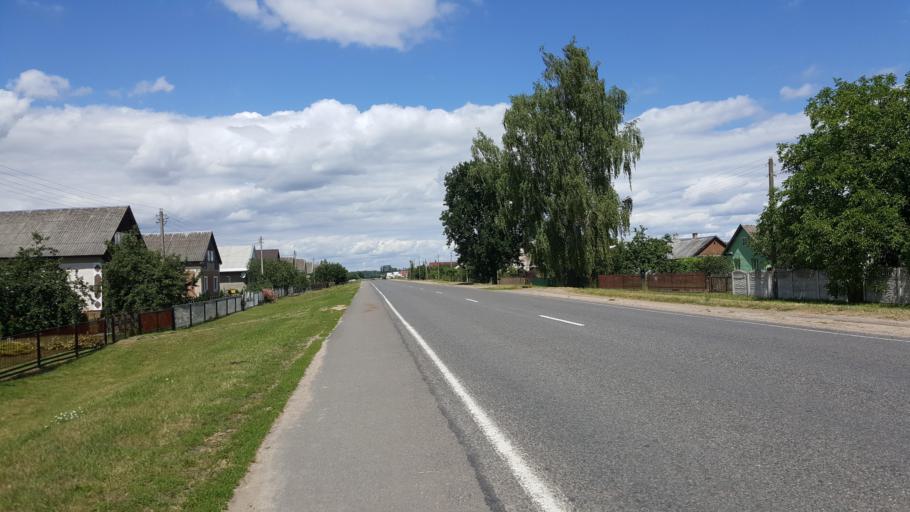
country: BY
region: Brest
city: Kamyanyets
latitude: 52.3208
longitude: 23.9186
